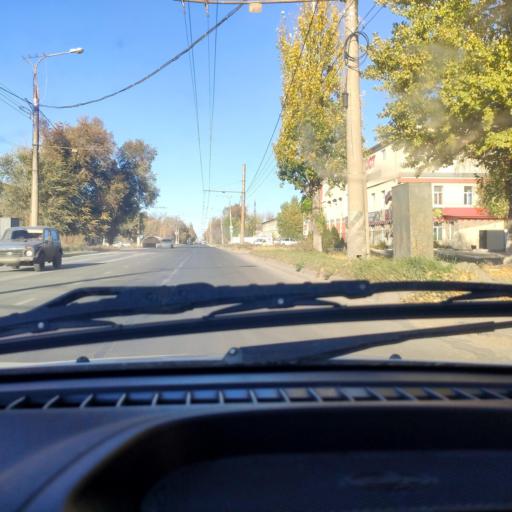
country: RU
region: Samara
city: Tol'yatti
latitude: 53.5618
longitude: 49.4547
